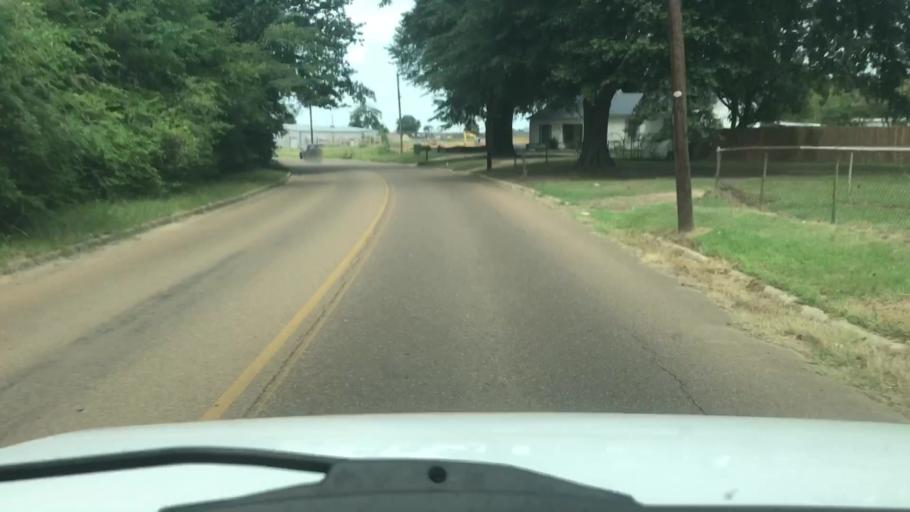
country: US
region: Texas
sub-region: Bowie County
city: Wake Village
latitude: 33.4425
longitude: -94.0903
